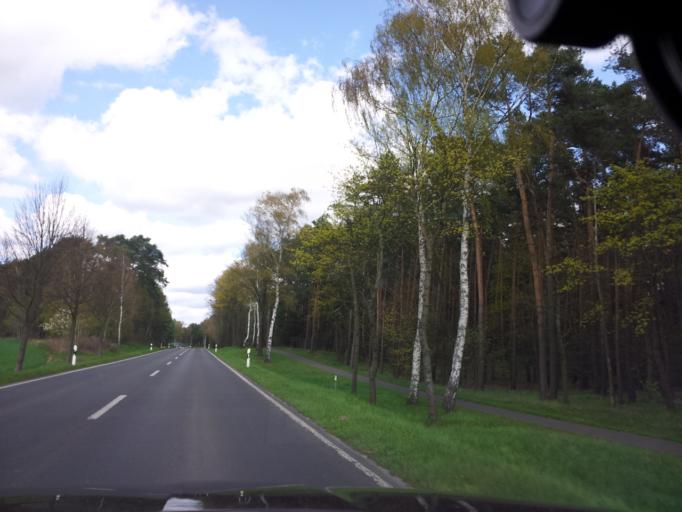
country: DE
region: Brandenburg
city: Rudnitz
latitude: 52.7021
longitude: 13.6111
